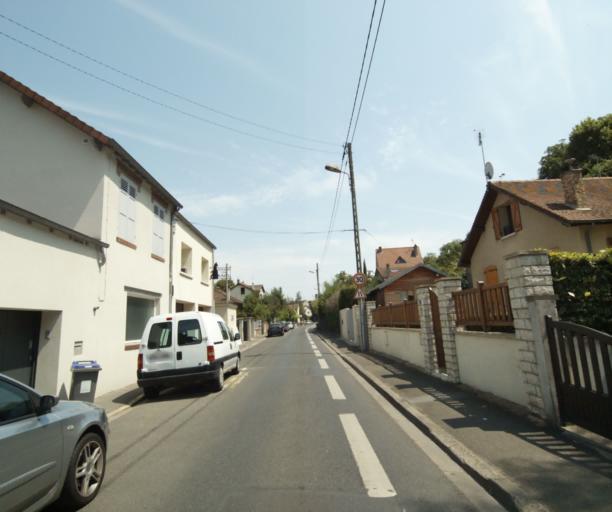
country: FR
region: Ile-de-France
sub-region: Departement des Yvelines
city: Conflans-Sainte-Honorine
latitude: 48.9947
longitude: 2.0982
